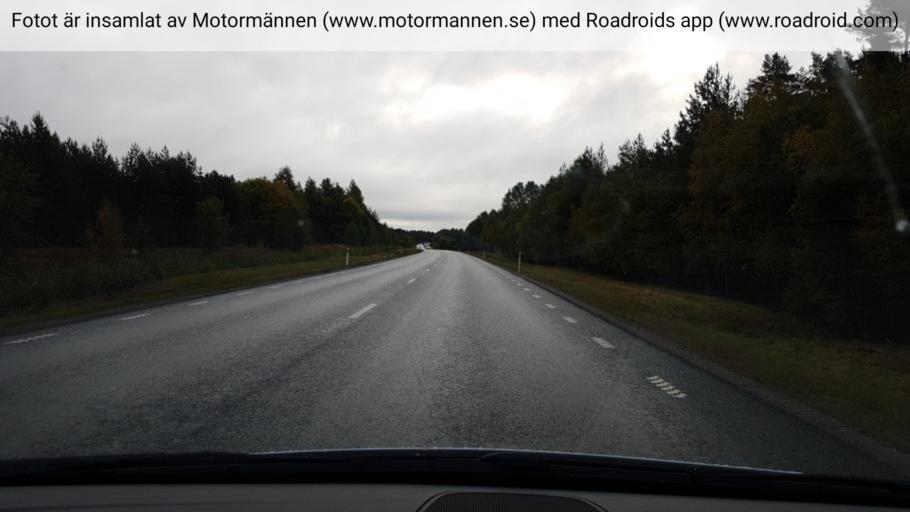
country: SE
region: Vaesterbotten
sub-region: Umea Kommun
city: Roback
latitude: 63.8481
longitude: 20.1312
